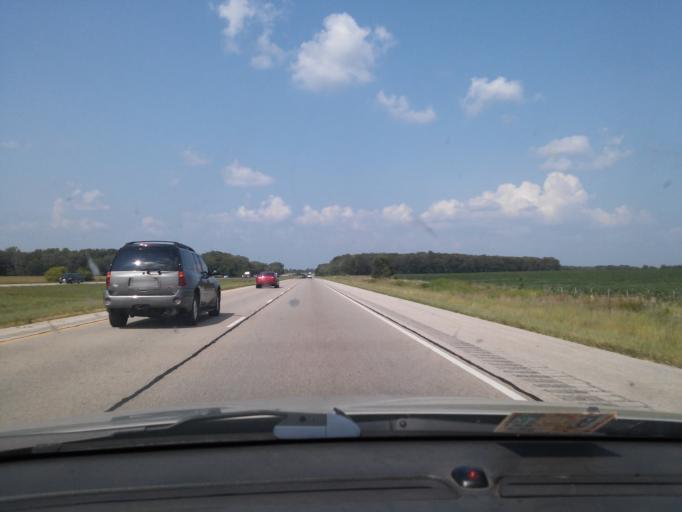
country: US
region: Illinois
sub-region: McLean County
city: Twin Grove
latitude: 40.3661
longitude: -89.1027
